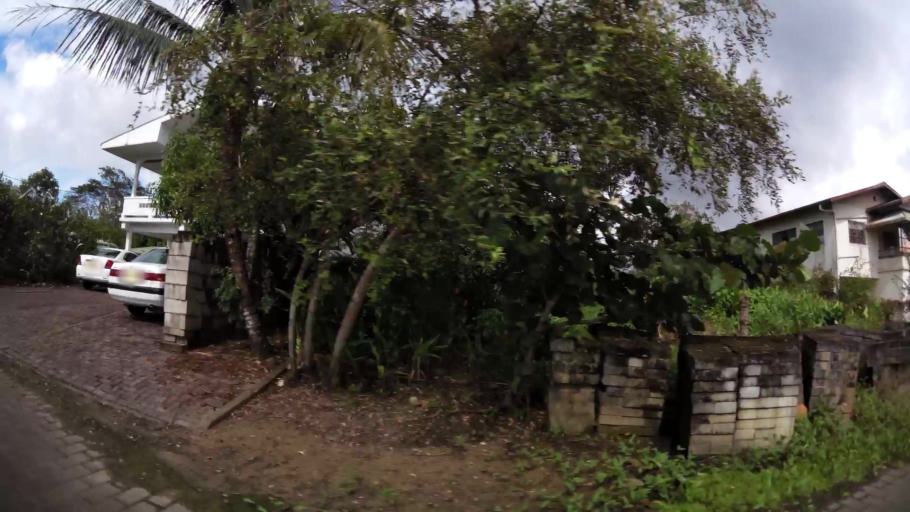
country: SR
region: Paramaribo
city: Paramaribo
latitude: 5.8451
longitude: -55.1910
